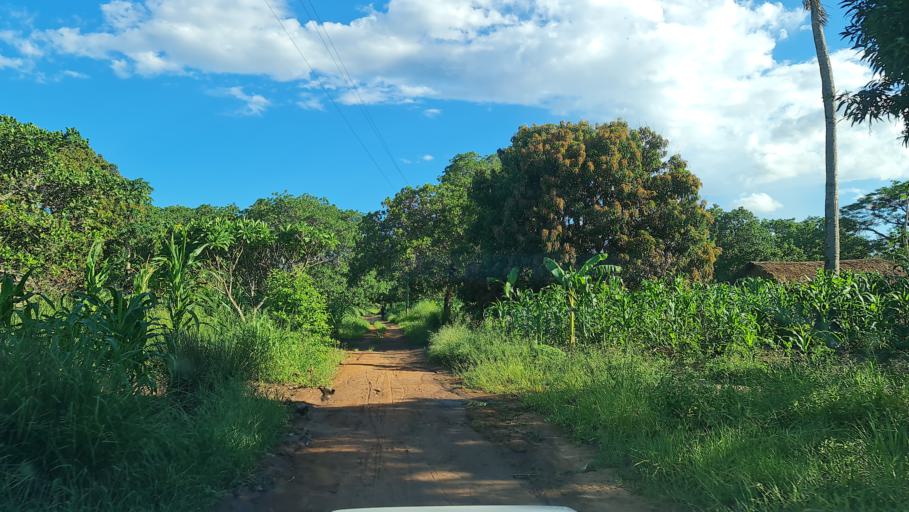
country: MZ
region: Nampula
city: Ilha de Mocambique
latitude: -14.9272
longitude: 40.2199
